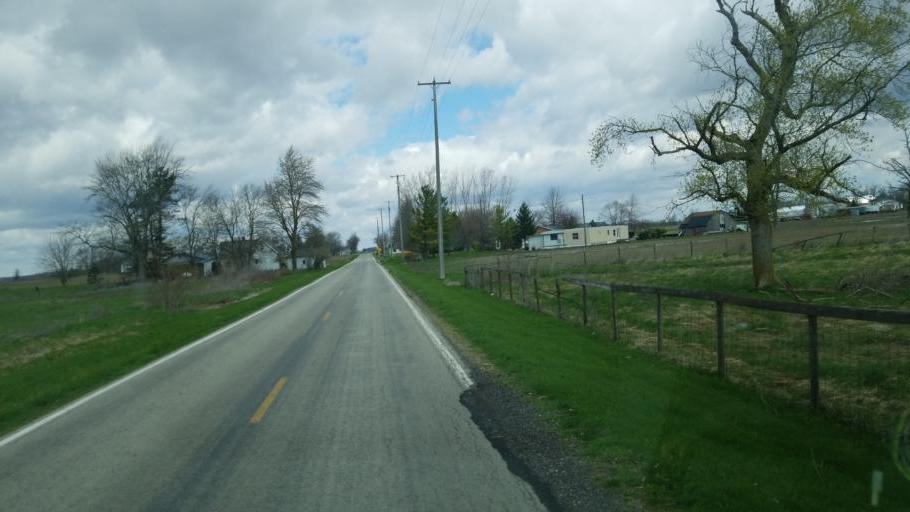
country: US
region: Ohio
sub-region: Union County
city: Richwood
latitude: 40.4210
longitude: -83.3106
